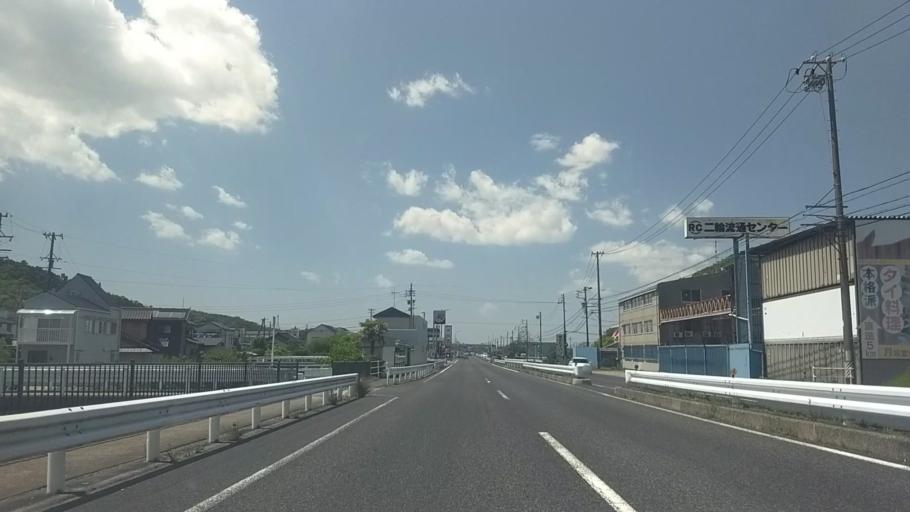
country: JP
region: Aichi
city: Okazaki
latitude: 34.9127
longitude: 137.2224
